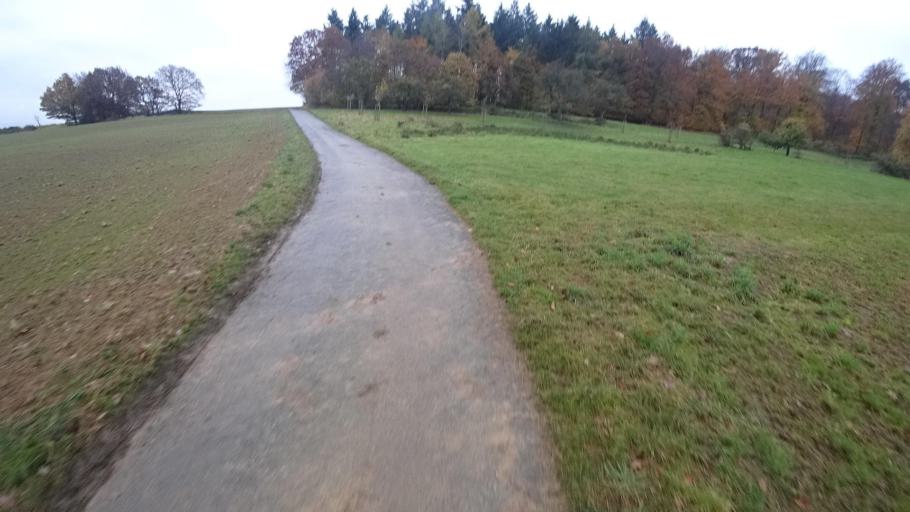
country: DE
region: Rheinland-Pfalz
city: Sankt Goar
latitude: 50.1382
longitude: 7.6951
